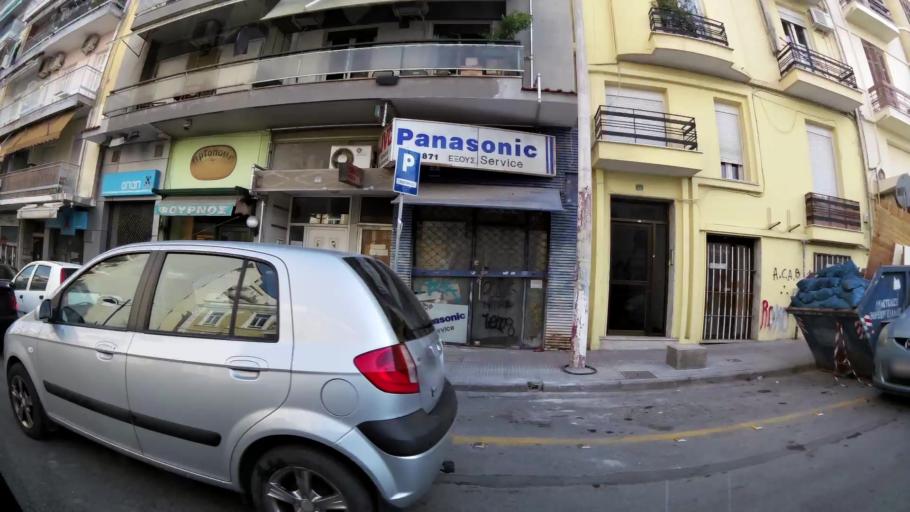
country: GR
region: Central Macedonia
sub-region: Nomos Thessalonikis
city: Sykies
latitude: 40.6399
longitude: 22.9473
